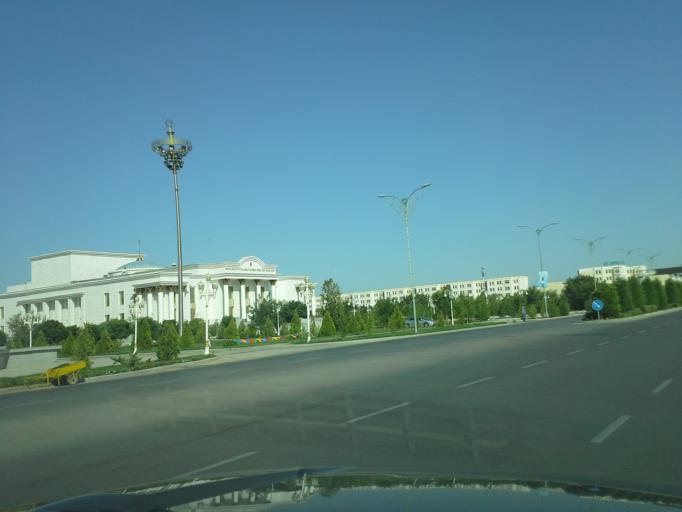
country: TM
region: Dasoguz
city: Dasoguz
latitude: 41.8248
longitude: 59.9613
